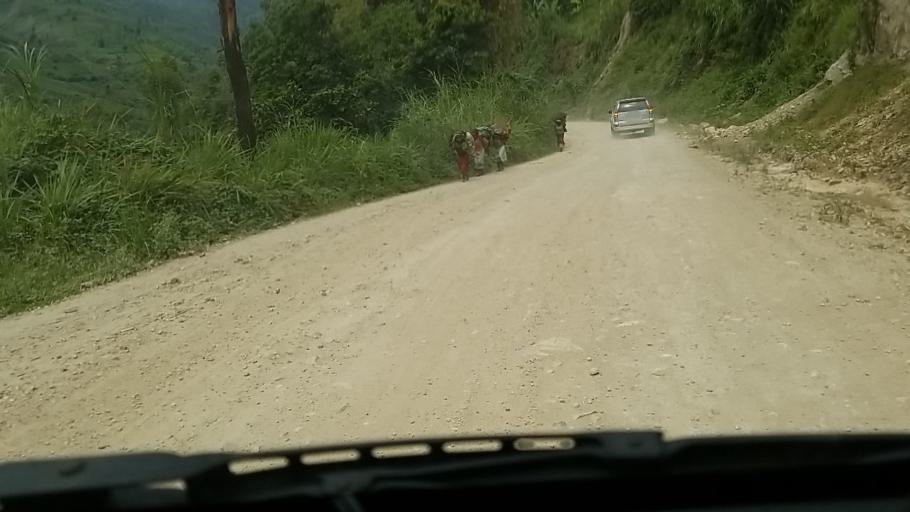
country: CD
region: Nord Kivu
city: Sake
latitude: -1.5903
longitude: 29.0442
